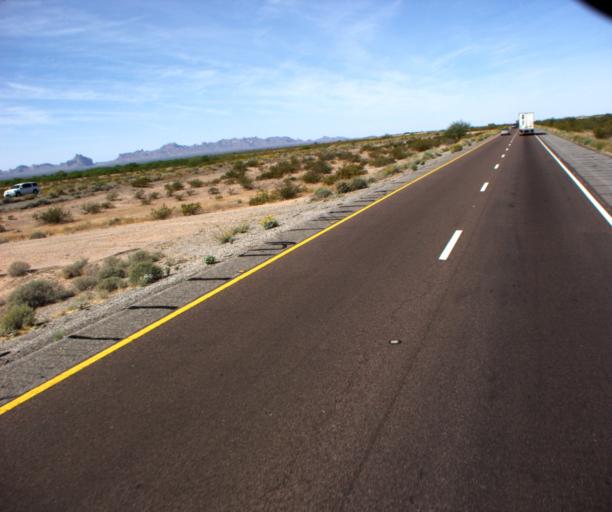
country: US
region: Arizona
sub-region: La Paz County
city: Salome
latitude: 33.5450
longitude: -113.1934
